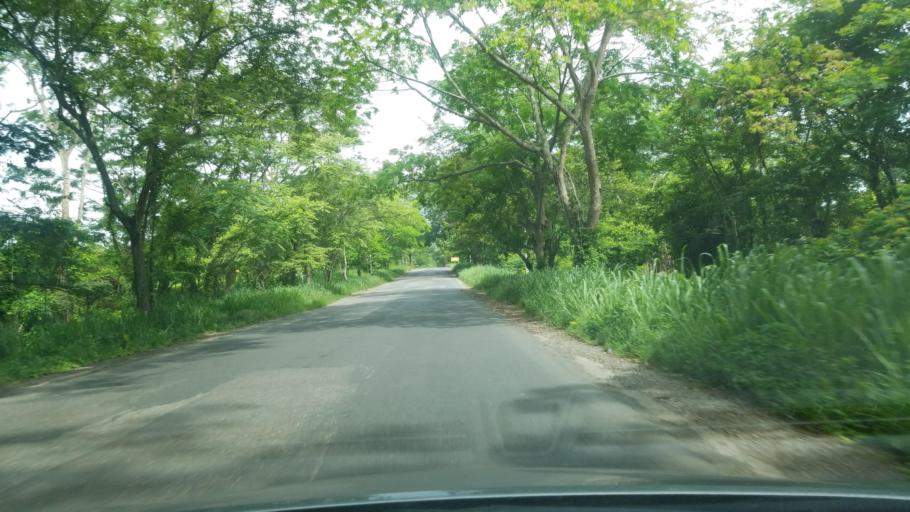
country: HN
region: Santa Barbara
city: Camalote
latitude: 15.3343
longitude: -88.3493
